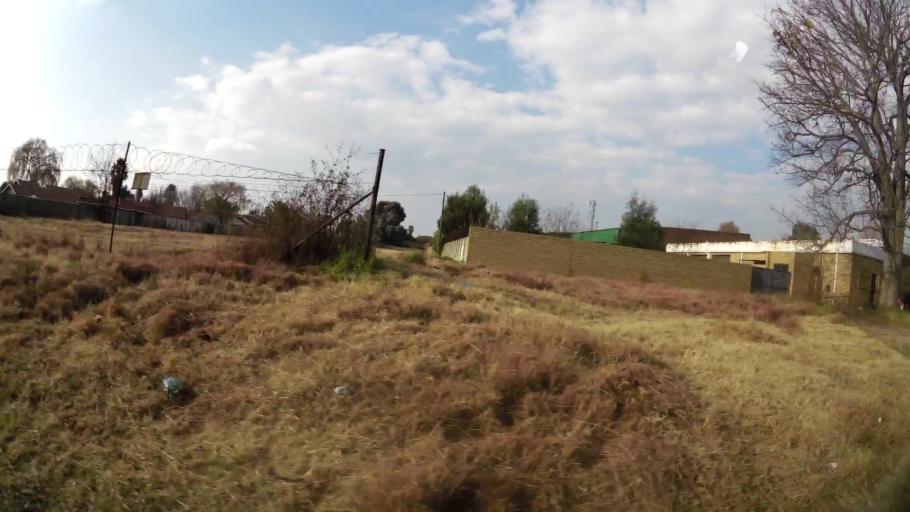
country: ZA
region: Gauteng
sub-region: Ekurhuleni Metropolitan Municipality
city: Benoni
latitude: -26.1242
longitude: 28.3711
